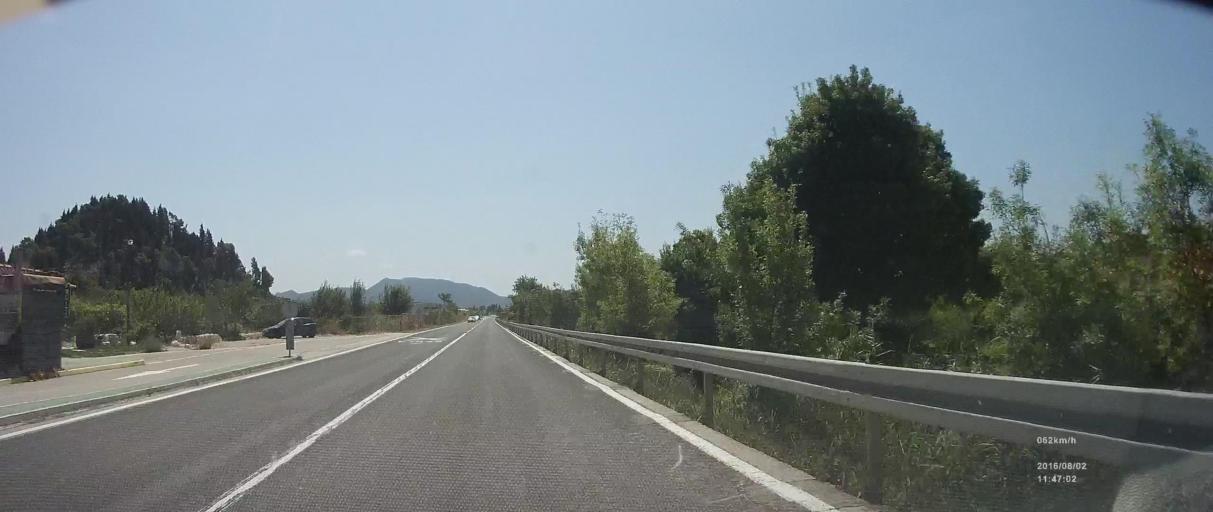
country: HR
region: Dubrovacko-Neretvanska
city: Komin
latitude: 43.0480
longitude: 17.4793
